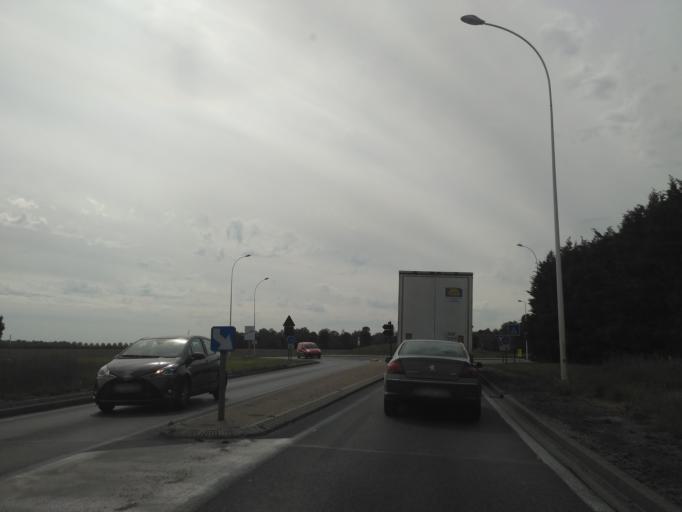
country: FR
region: Ile-de-France
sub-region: Departement de Seine-et-Marne
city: Soignolles-en-Brie
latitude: 48.6308
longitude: 2.6642
